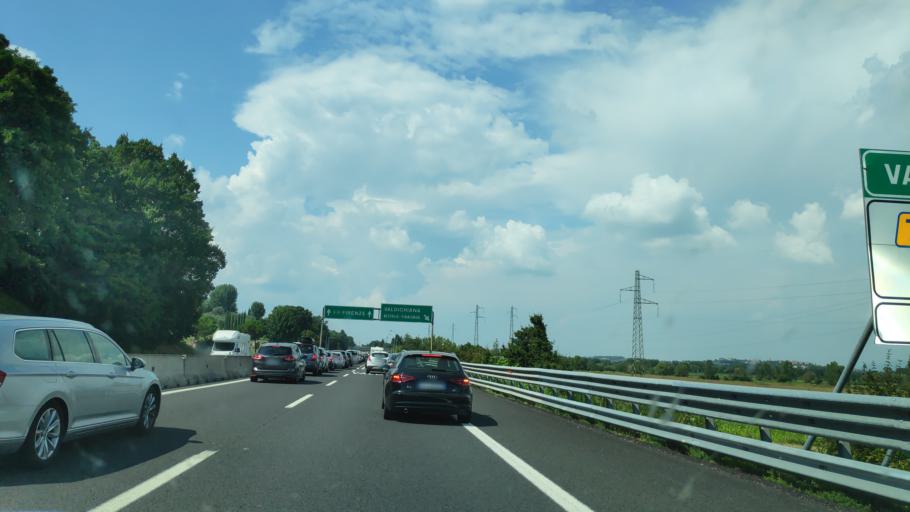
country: IT
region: Tuscany
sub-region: Provincia di Siena
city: Bettolle
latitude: 43.2078
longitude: 11.8120
